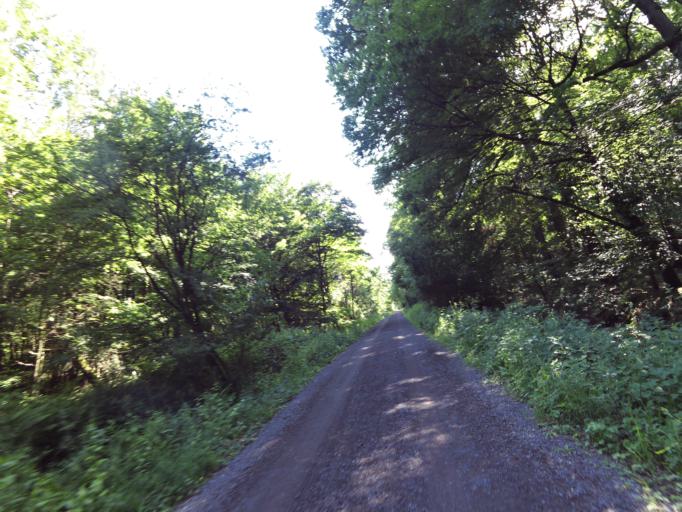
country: DE
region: North Rhine-Westphalia
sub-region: Regierungsbezirk Koln
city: Wachtberg
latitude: 50.6821
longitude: 7.1128
